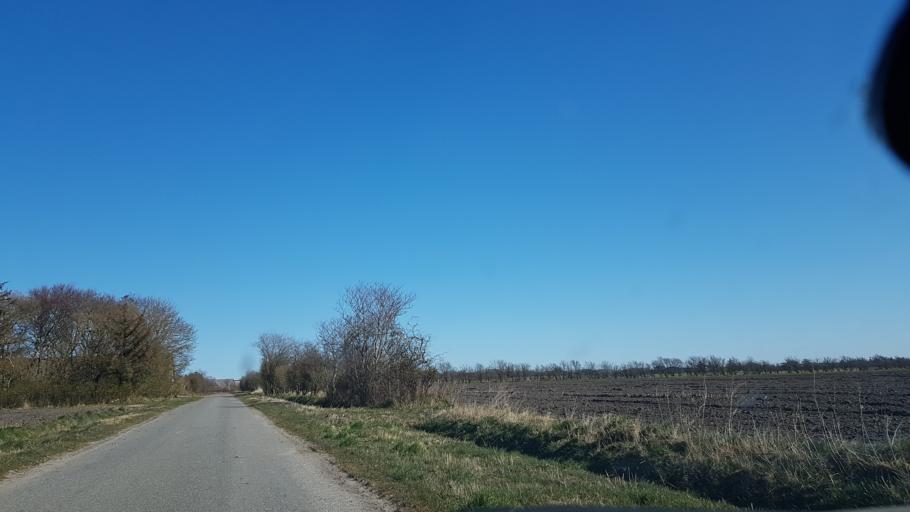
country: DK
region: South Denmark
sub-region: Tonder Kommune
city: Sherrebek
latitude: 55.2280
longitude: 8.7071
